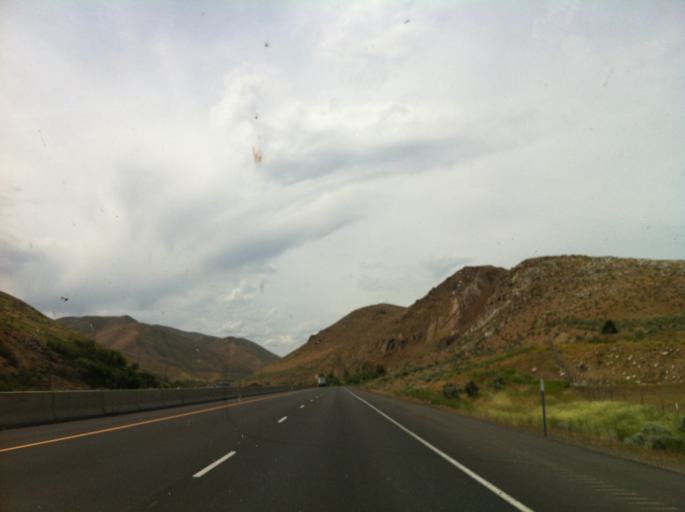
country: US
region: Idaho
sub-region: Washington County
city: Weiser
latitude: 44.3848
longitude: -117.3088
